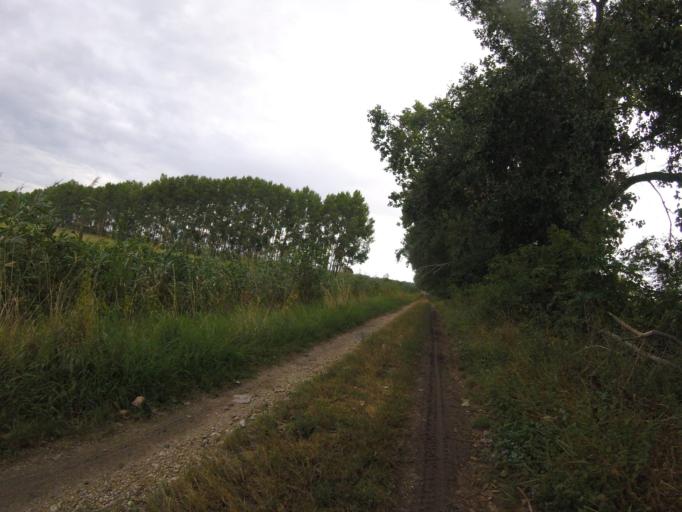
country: HU
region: Gyor-Moson-Sopron
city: Nagycenk
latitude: 47.6350
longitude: 16.7601
